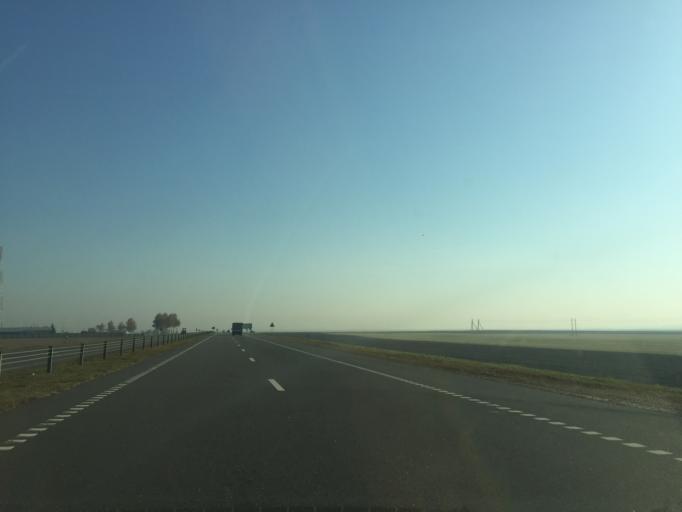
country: BY
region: Gomel
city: Kastsyukowka
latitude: 52.4939
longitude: 30.8462
